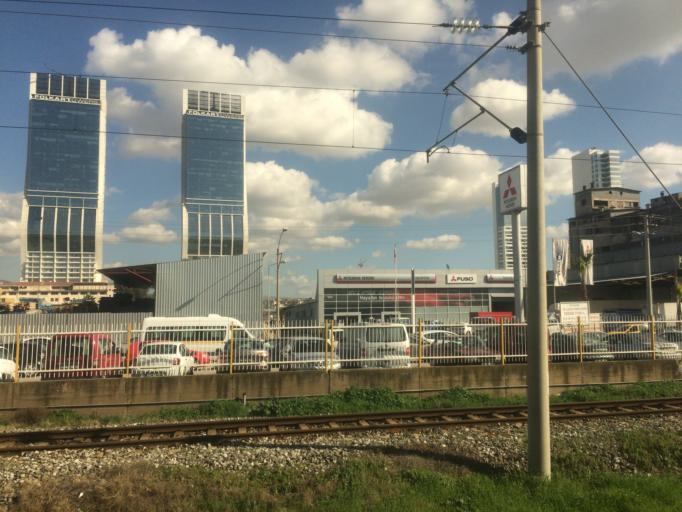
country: TR
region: Izmir
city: Izmir
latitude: 38.4521
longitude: 27.1717
